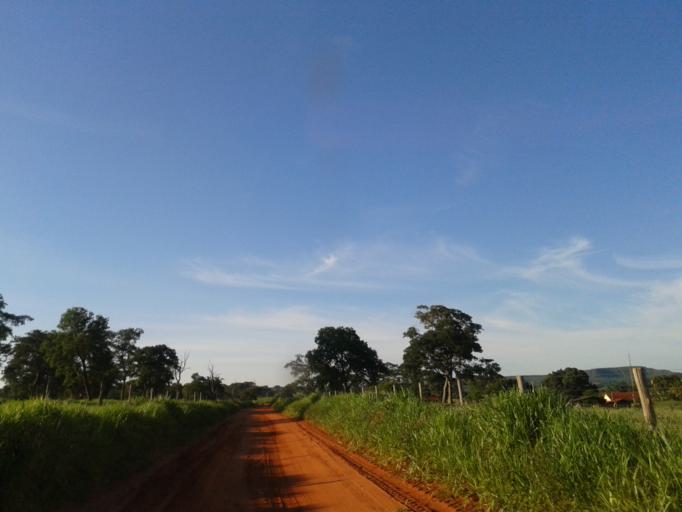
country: BR
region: Minas Gerais
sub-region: Santa Vitoria
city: Santa Vitoria
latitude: -18.9512
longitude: -49.8633
